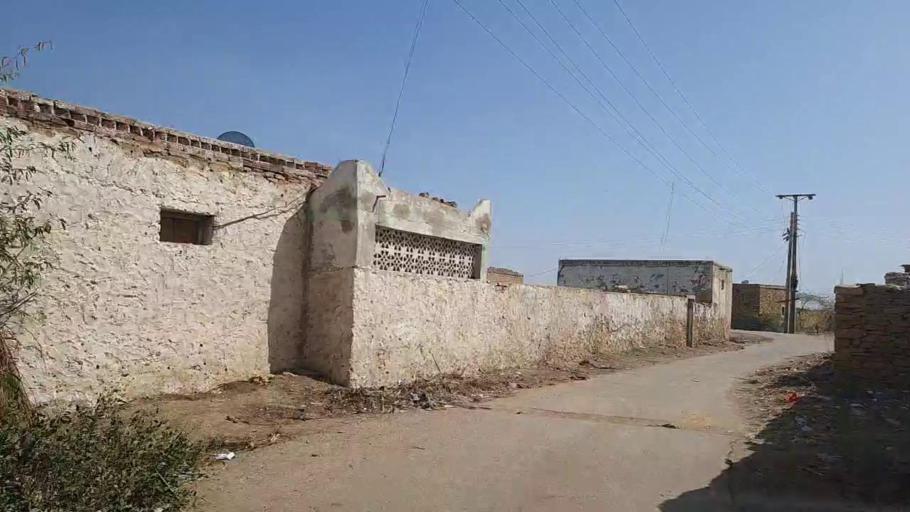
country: PK
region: Sindh
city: Kotri
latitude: 25.1517
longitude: 68.2391
